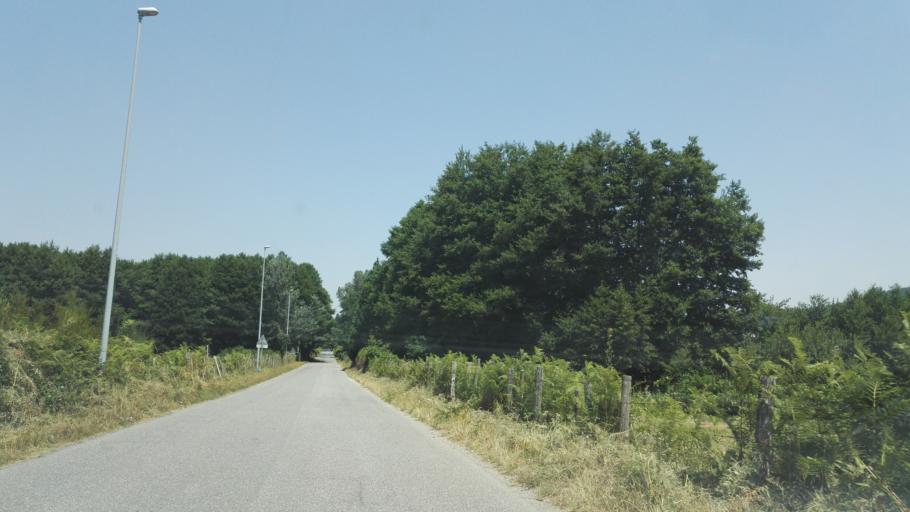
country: IT
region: Calabria
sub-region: Provincia di Vibo-Valentia
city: Mongiana
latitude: 38.5253
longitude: 16.3202
